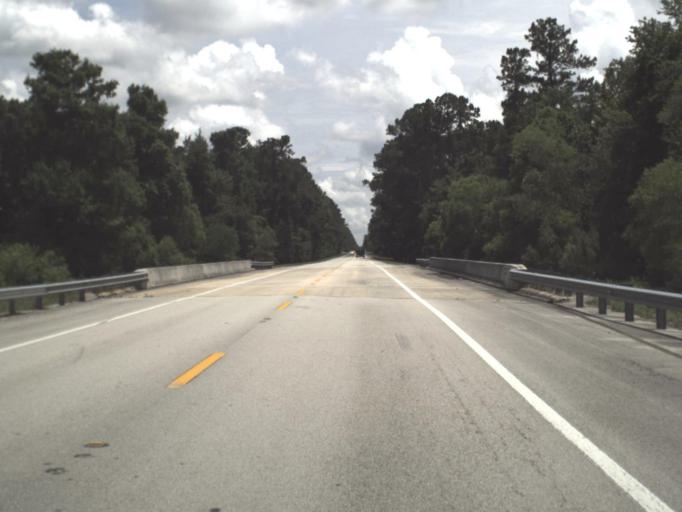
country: US
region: Florida
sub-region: Nassau County
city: Yulee
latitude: 30.6895
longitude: -81.6551
